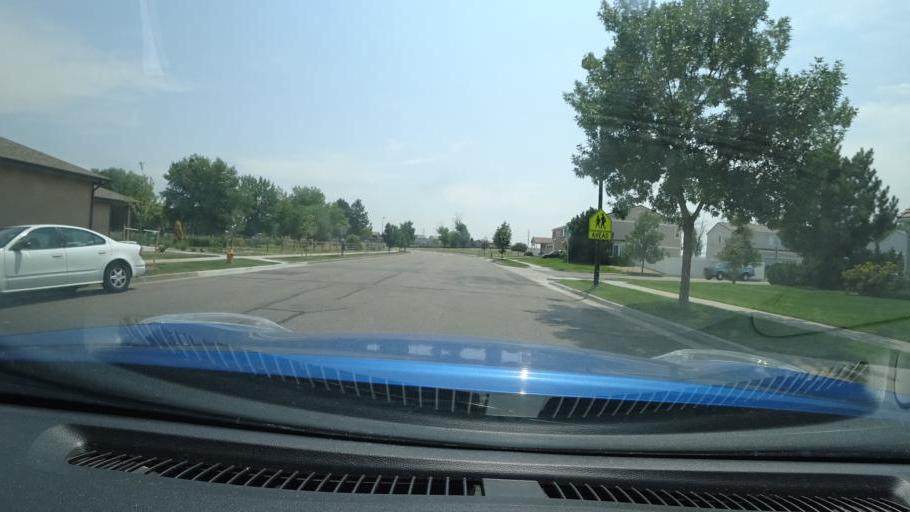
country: US
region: Colorado
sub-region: Adams County
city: Aurora
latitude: 39.7724
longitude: -104.7673
